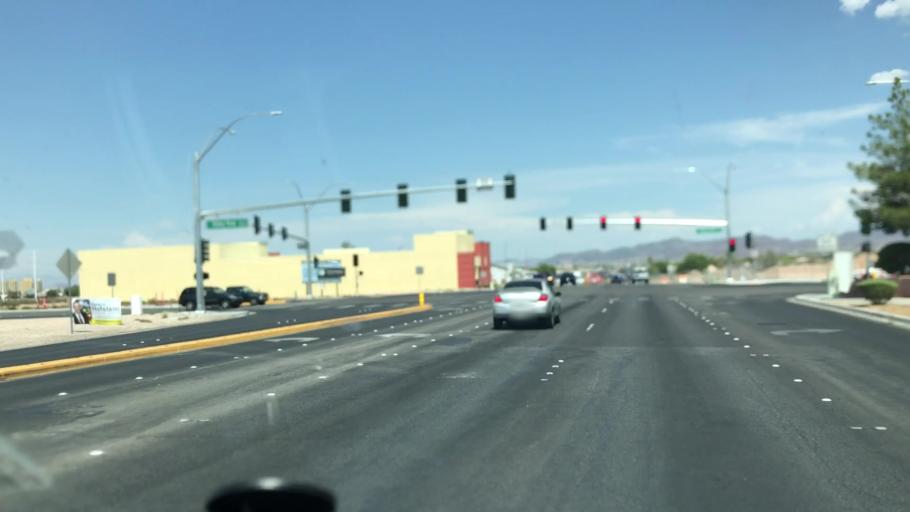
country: US
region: Nevada
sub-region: Clark County
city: Enterprise
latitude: 35.9988
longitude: -115.1903
